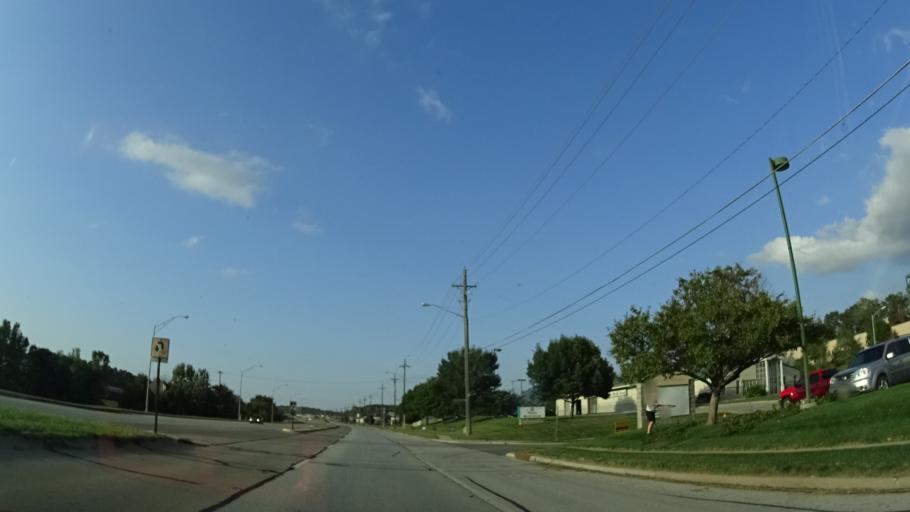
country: US
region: Nebraska
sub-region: Sarpy County
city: Offutt Air Force Base
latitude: 41.1606
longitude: -95.9251
